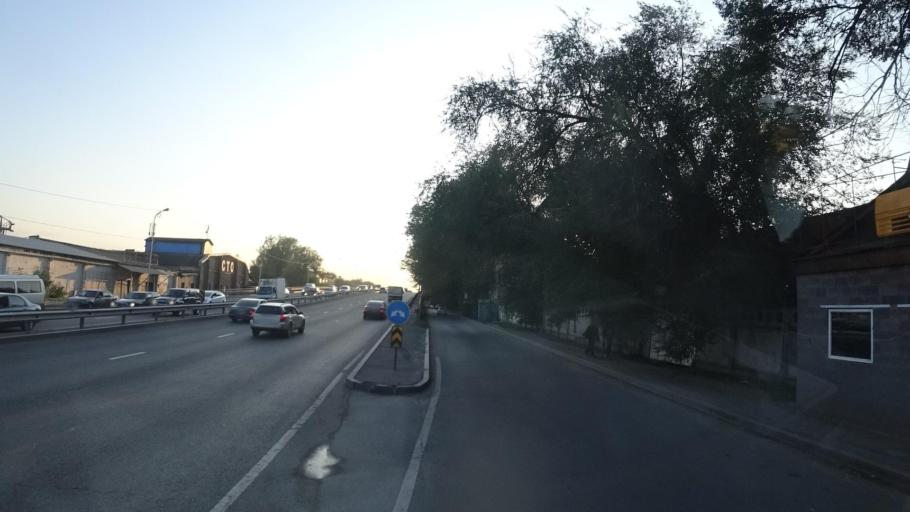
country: KZ
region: Almaty Qalasy
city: Almaty
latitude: 43.2815
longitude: 76.9141
